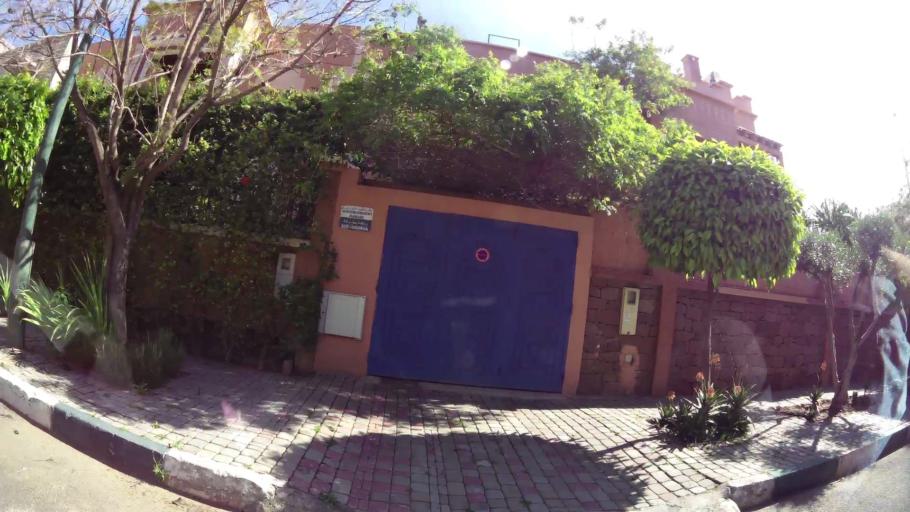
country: MA
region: Marrakech-Tensift-Al Haouz
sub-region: Marrakech
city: Marrakesh
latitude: 31.6528
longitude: -8.0569
